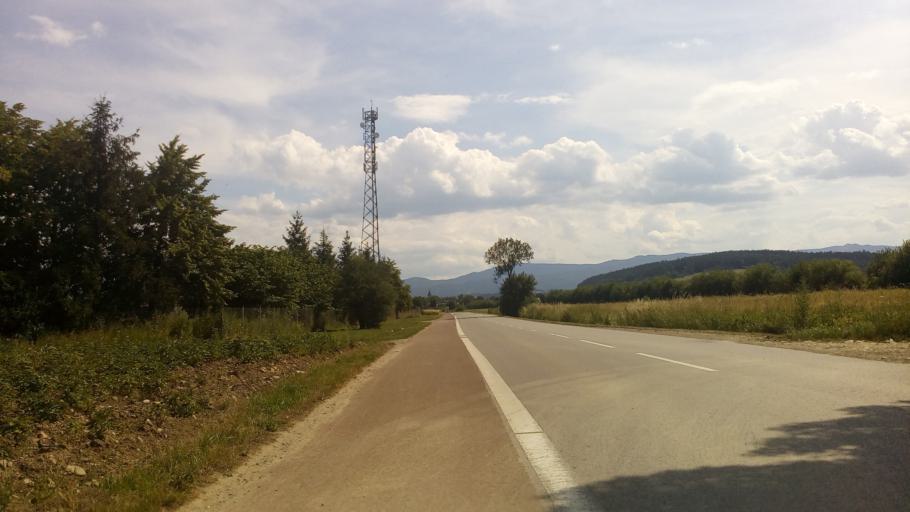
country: PL
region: Lesser Poland Voivodeship
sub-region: Powiat nowosadecki
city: Stary Sacz
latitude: 49.5769
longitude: 20.6364
